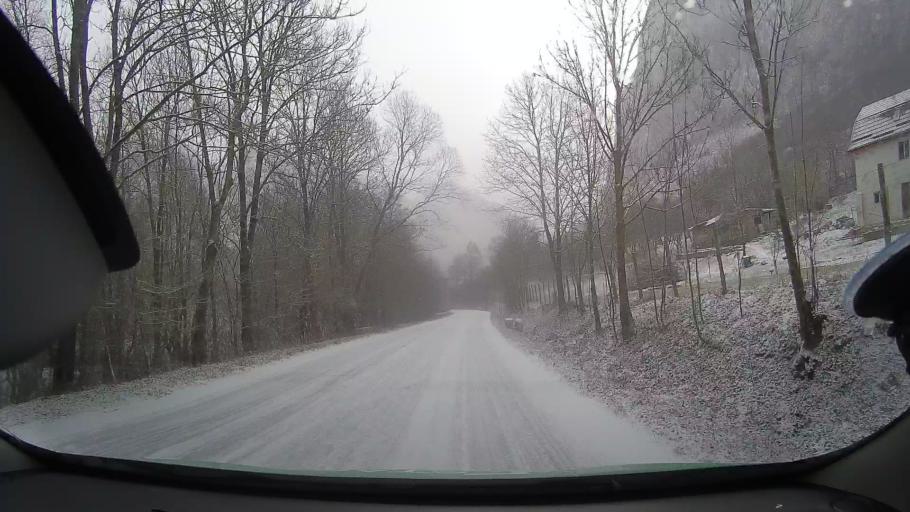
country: RO
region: Alba
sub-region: Comuna Livezile
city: Livezile
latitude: 46.3840
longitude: 23.5785
